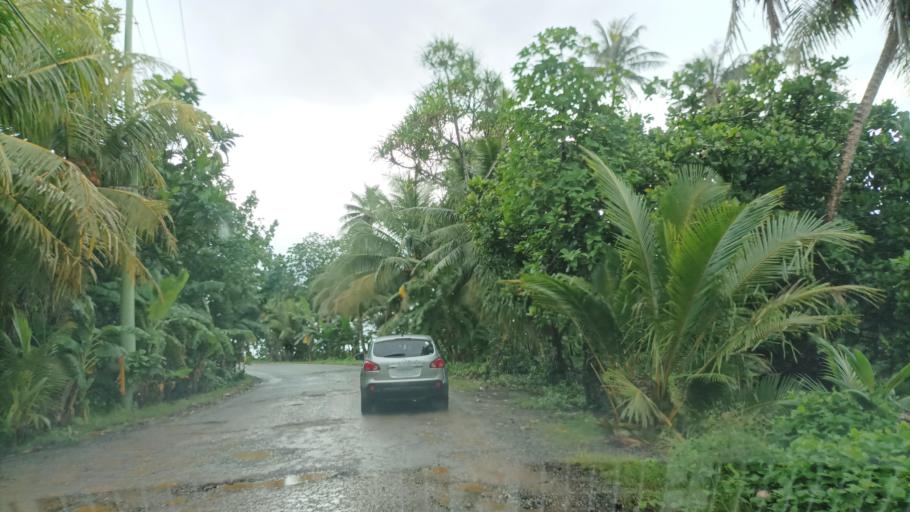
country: FM
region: Kosrae
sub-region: Lelu Municipality
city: Lelu
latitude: 5.3475
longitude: 163.0222
